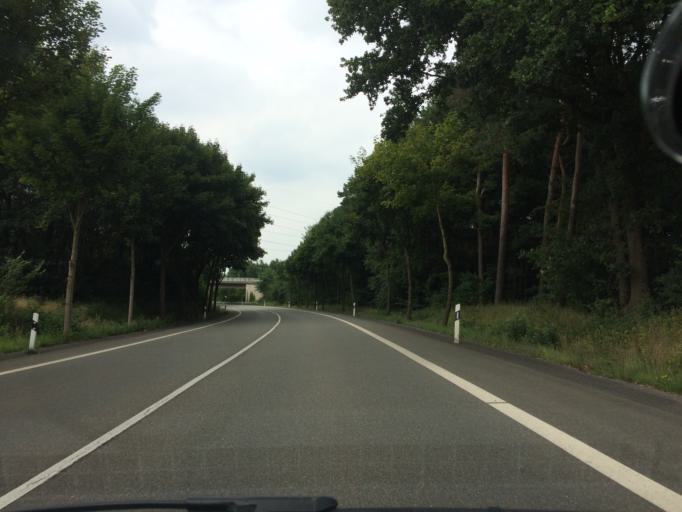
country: DE
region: North Rhine-Westphalia
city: Marl
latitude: 51.7072
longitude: 7.0652
